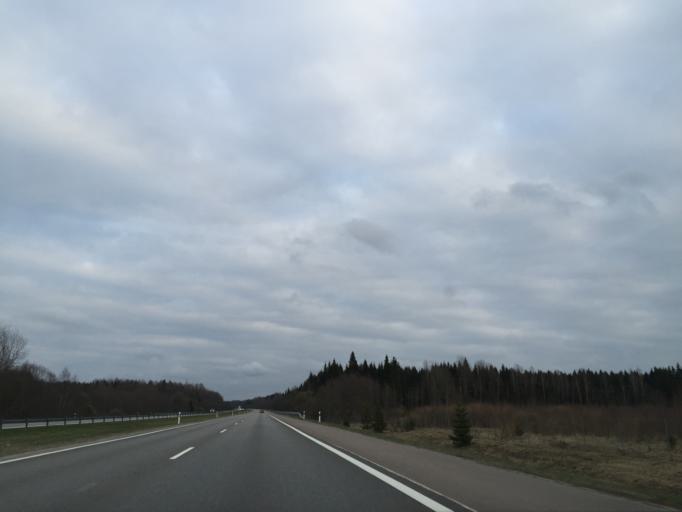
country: LT
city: Rietavas
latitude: 55.6402
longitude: 21.8953
